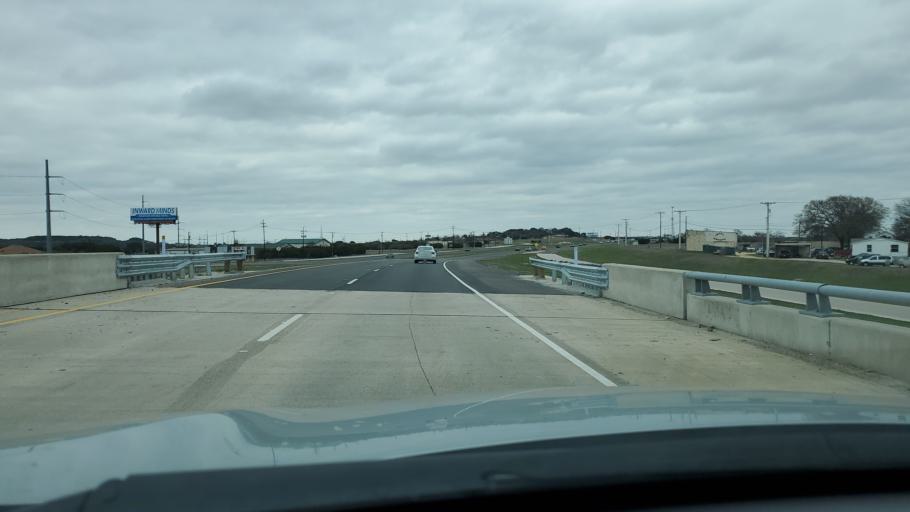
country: US
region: Texas
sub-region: Bell County
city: Killeen
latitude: 31.0576
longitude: -97.7655
